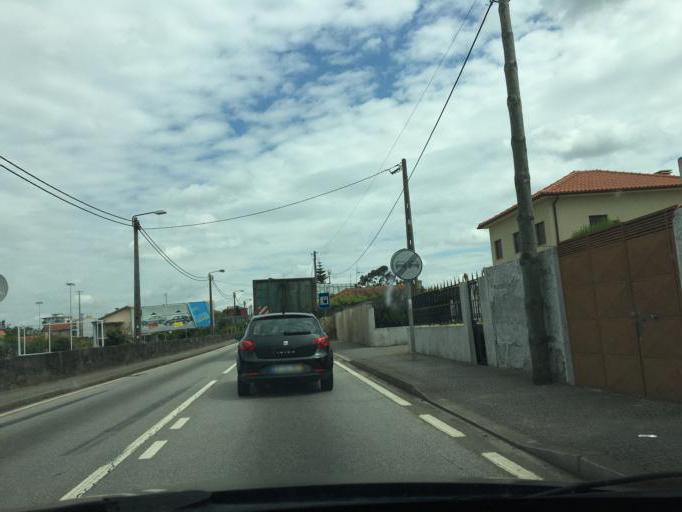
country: PT
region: Porto
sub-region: Maia
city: Anta
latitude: 41.2552
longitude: -8.6165
